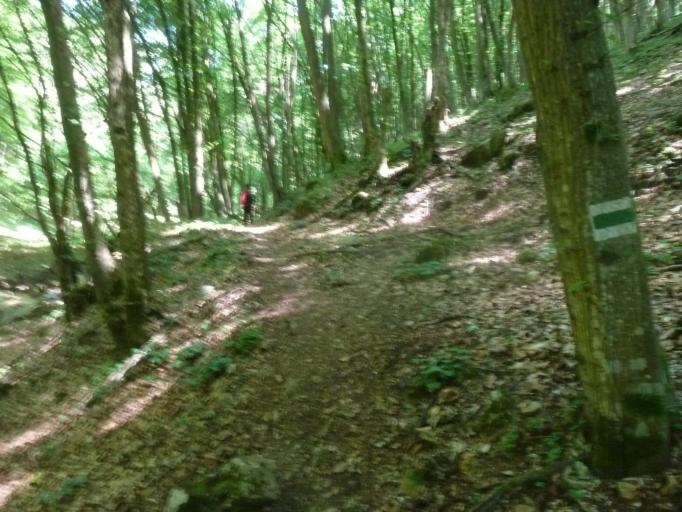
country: HU
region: Borsod-Abauj-Zemplen
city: Rudabanya
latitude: 48.4871
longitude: 20.5175
